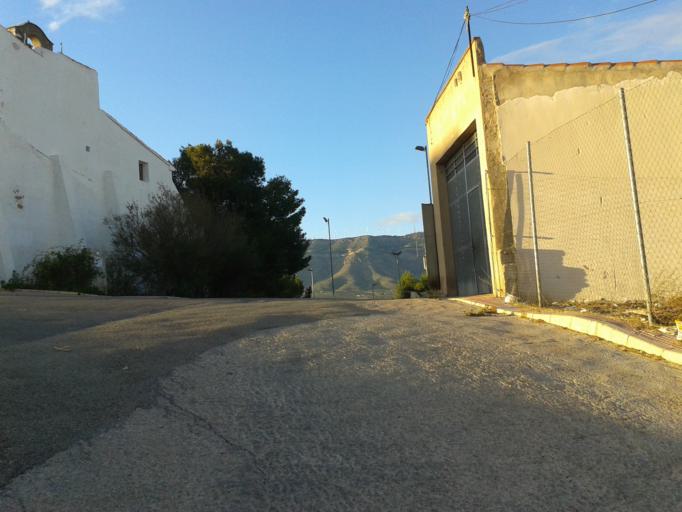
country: ES
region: Castille-La Mancha
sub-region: Provincia de Albacete
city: Caudete
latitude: 38.7047
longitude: -0.9913
